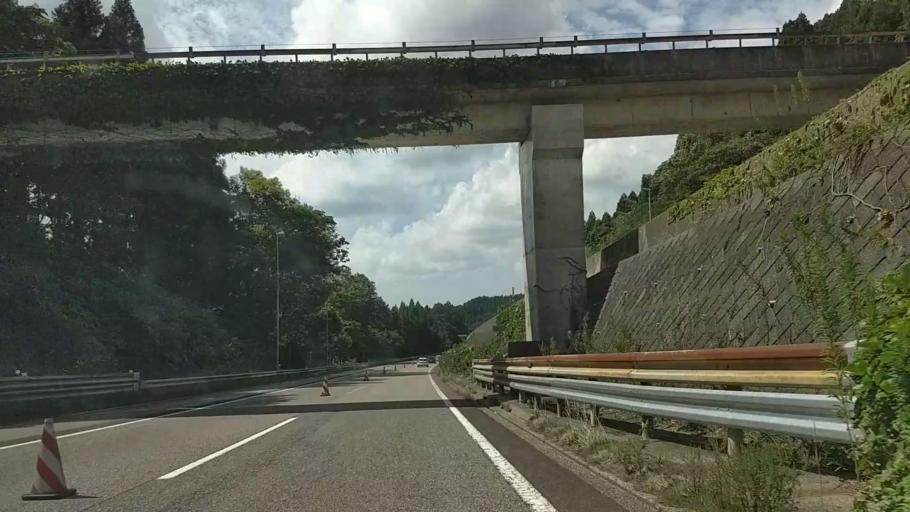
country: JP
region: Ishikawa
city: Tsubata
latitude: 36.5970
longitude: 136.7687
